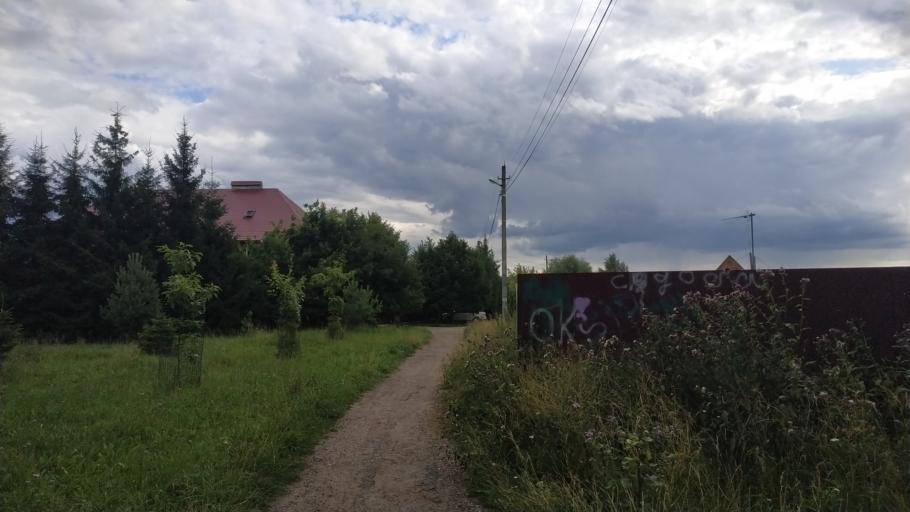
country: RU
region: Moskovskaya
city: Istra
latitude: 55.8985
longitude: 36.8560
